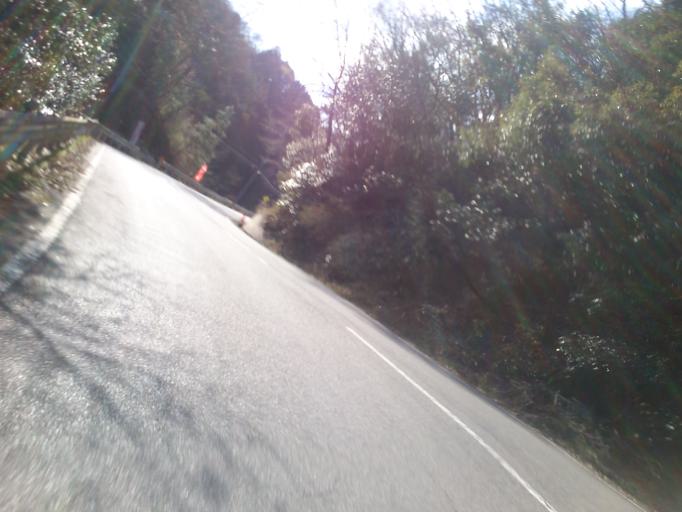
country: JP
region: Kyoto
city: Yawata
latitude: 34.9145
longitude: 135.6590
